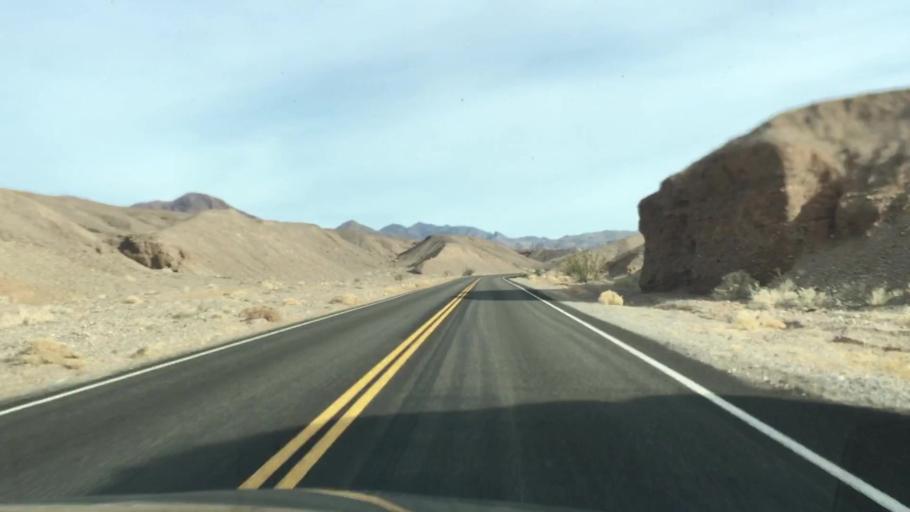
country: US
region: Nevada
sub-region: Nye County
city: Beatty
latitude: 36.6666
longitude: -117.0170
